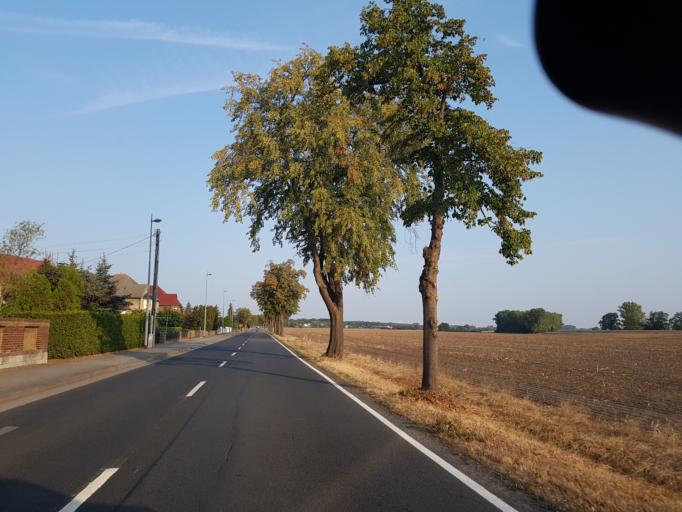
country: DE
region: Saxony-Anhalt
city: Pretzsch
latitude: 51.7194
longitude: 12.7980
